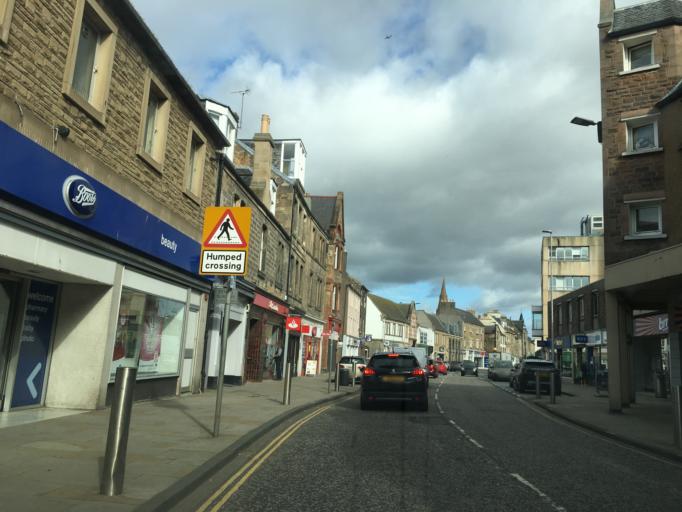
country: GB
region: Scotland
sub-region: Midlothian
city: Dalkeith
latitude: 55.8935
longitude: -3.0720
